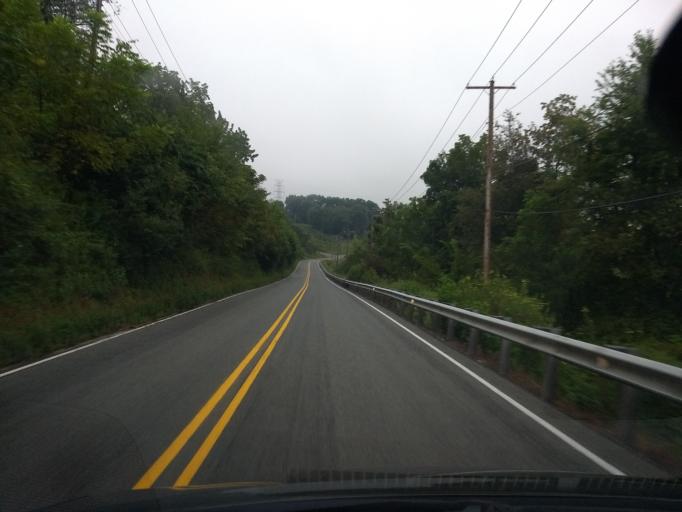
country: US
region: Pennsylvania
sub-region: Westmoreland County
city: Greensburg
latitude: 40.3206
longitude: -79.4878
